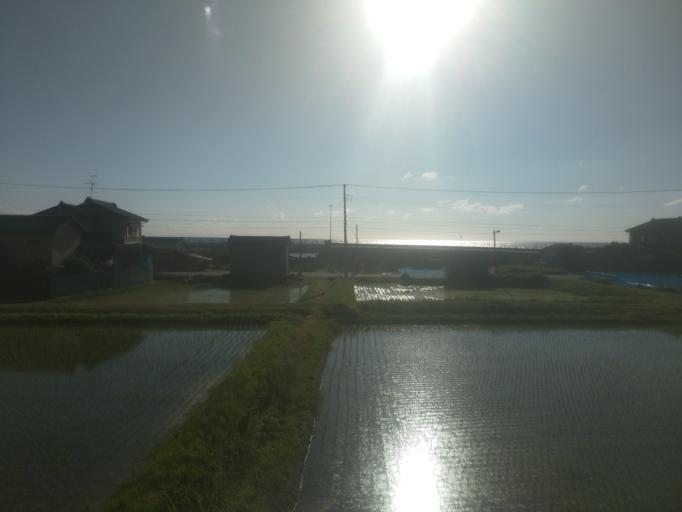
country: JP
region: Niigata
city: Murakami
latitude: 38.2785
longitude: 139.4508
